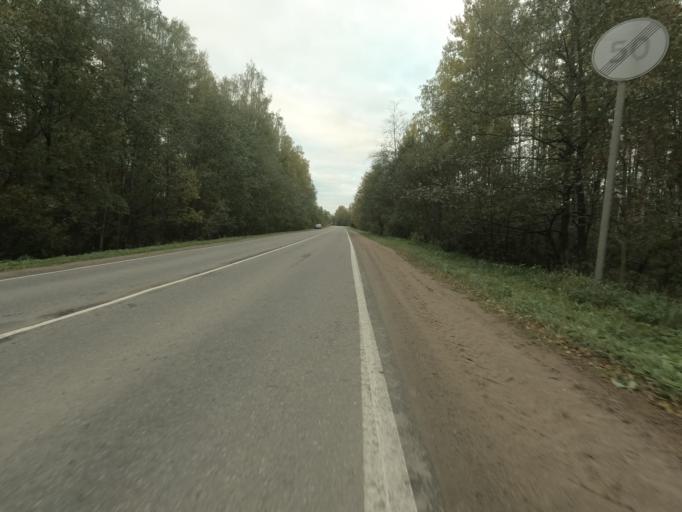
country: RU
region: Leningrad
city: Pavlovo
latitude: 59.8015
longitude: 30.9407
